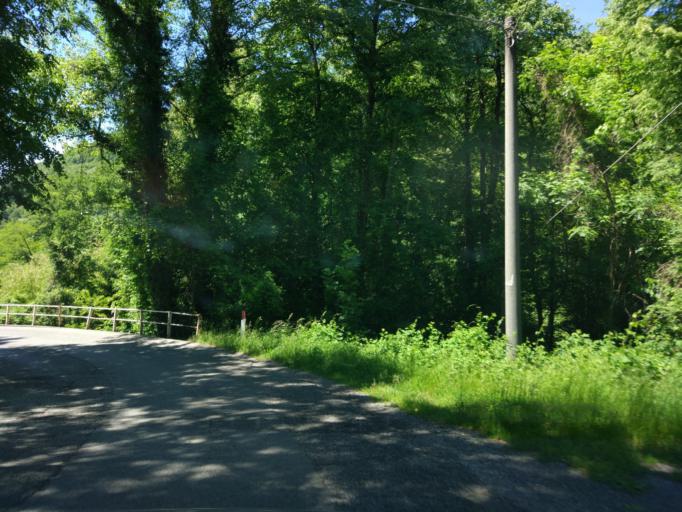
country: IT
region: Lombardy
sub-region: Provincia di Lecco
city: Taceno
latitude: 46.0243
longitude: 9.3695
